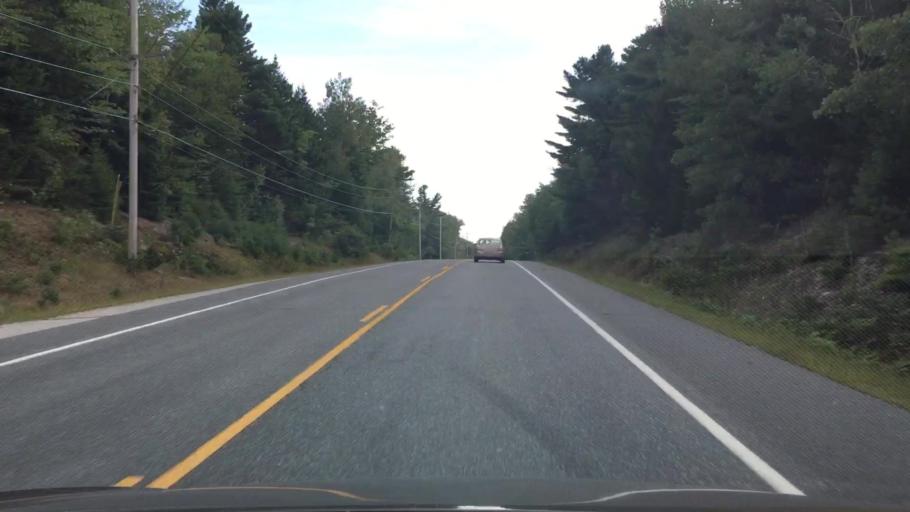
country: US
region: Maine
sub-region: Hancock County
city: Surry
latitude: 44.4473
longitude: -68.5607
